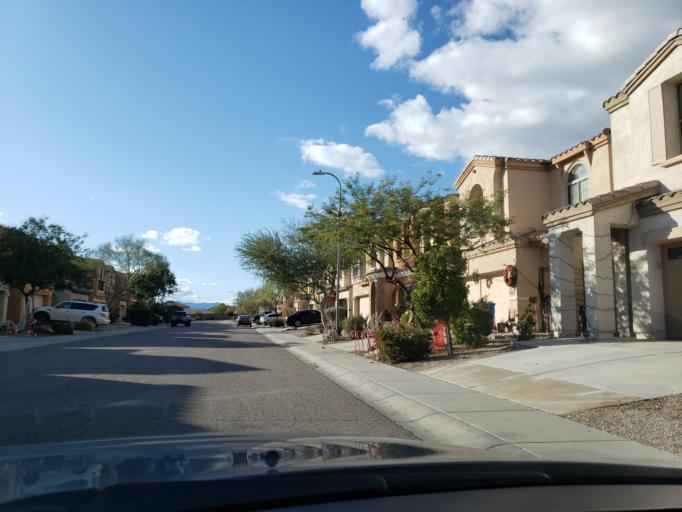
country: US
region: Arizona
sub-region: Maricopa County
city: Laveen
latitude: 33.2938
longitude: -112.0955
